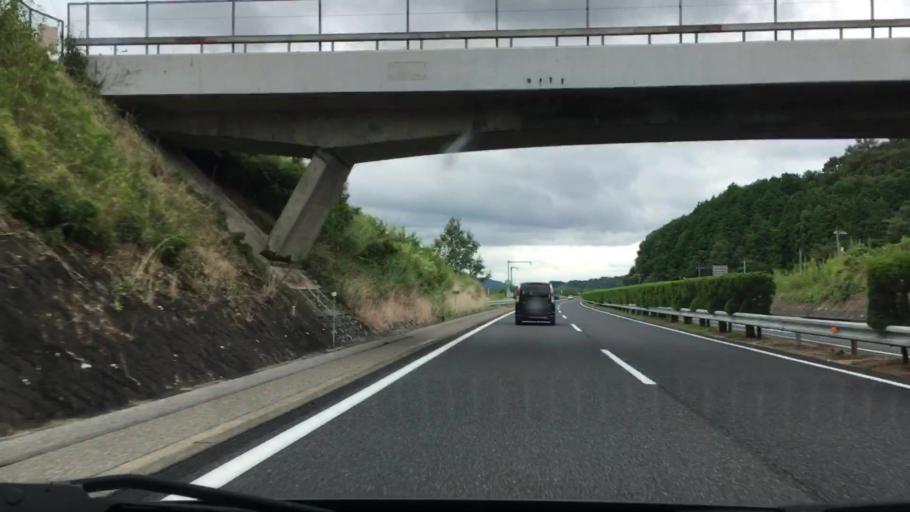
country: JP
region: Okayama
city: Tsuyama
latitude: 35.0447
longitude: 134.0845
